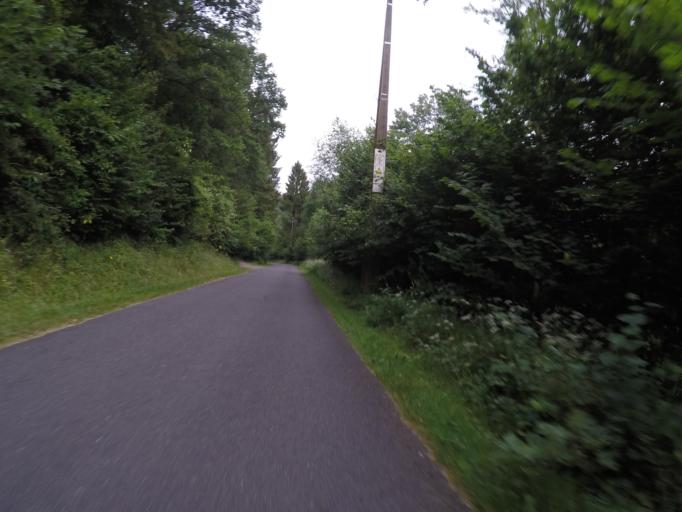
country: BE
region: Wallonia
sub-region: Province de Namur
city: Assesse
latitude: 50.3282
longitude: 4.9763
